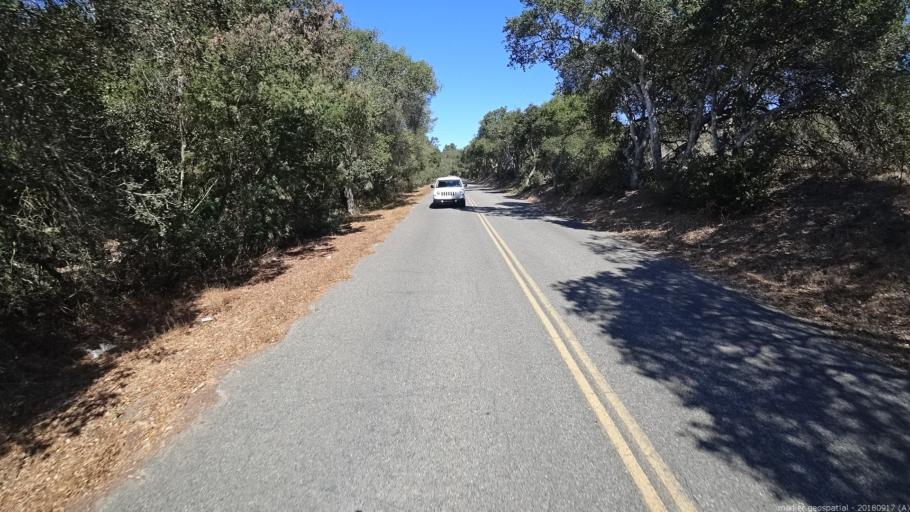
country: US
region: California
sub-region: Monterey County
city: Elkhorn
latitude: 36.8341
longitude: -121.6955
